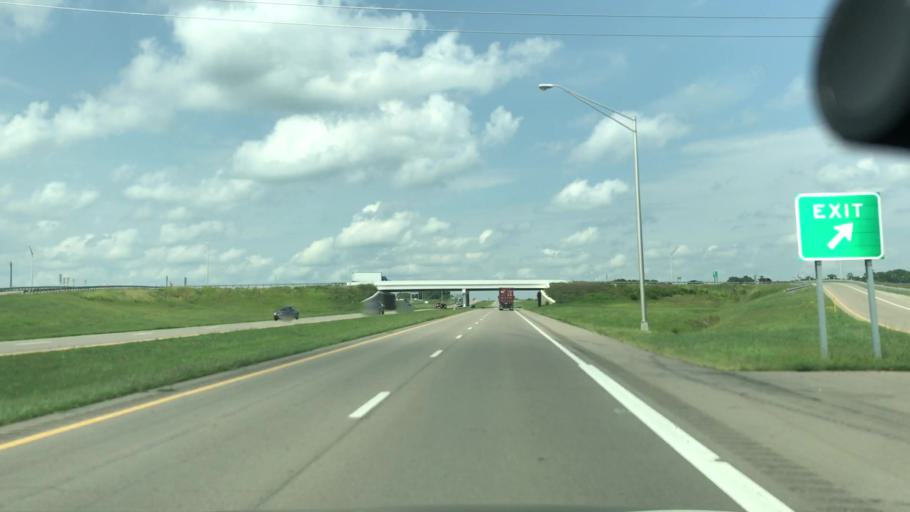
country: US
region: Ohio
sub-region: Ross County
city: Chillicothe
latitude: 39.4137
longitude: -82.9756
